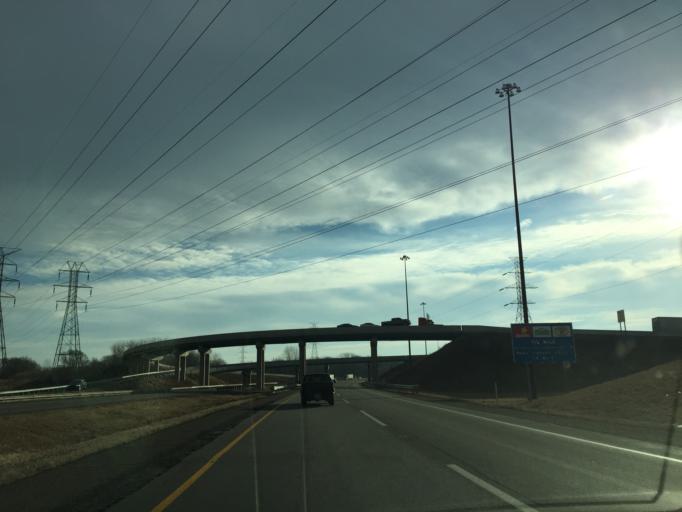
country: US
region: Indiana
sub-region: Lake County
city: Lake Station
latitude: 41.5930
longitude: -87.2354
